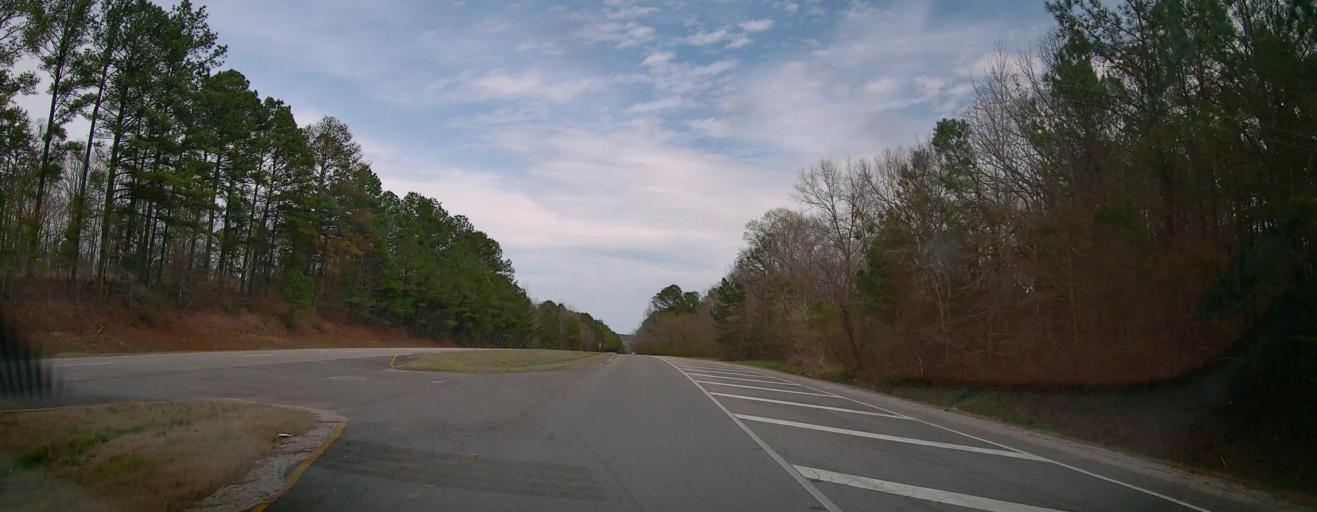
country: US
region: Alabama
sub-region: Marion County
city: Winfield
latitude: 33.9300
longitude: -87.7524
